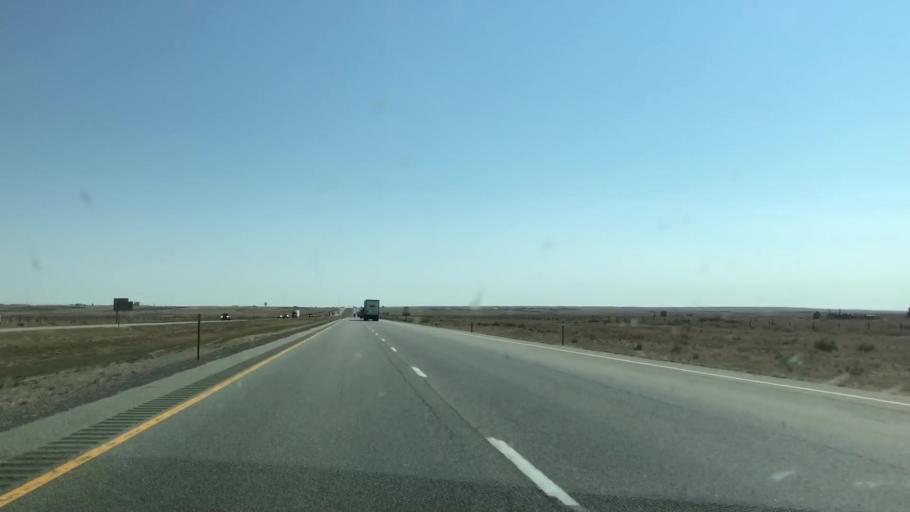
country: US
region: Wyoming
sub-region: Carbon County
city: Rawlins
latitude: 41.6664
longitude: -108.0232
